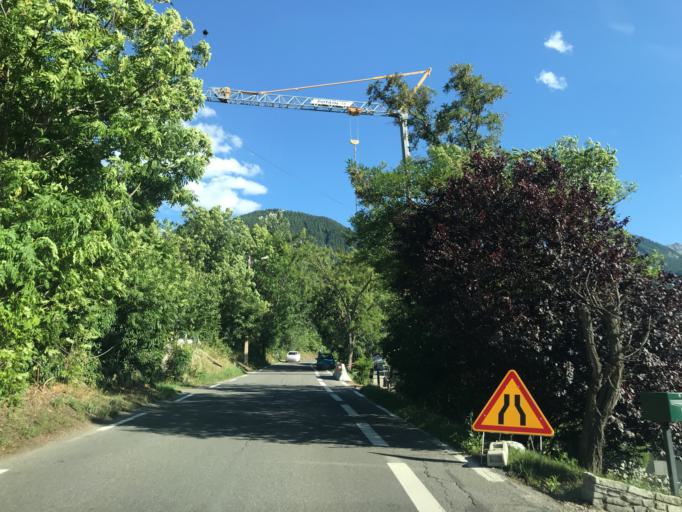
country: FR
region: Provence-Alpes-Cote d'Azur
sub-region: Departement des Hautes-Alpes
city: Briancon
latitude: 44.8913
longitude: 6.6383
